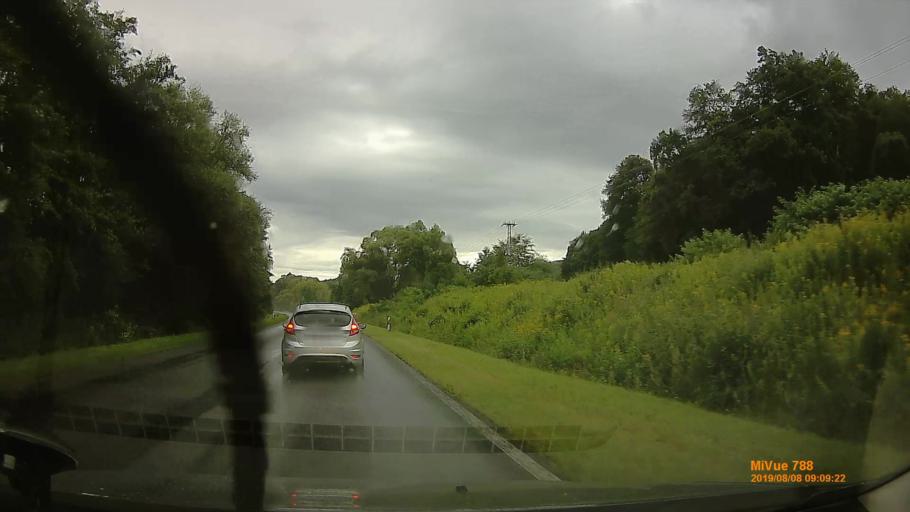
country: HU
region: Zala
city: Zalaegerszeg
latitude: 46.7557
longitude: 16.8578
